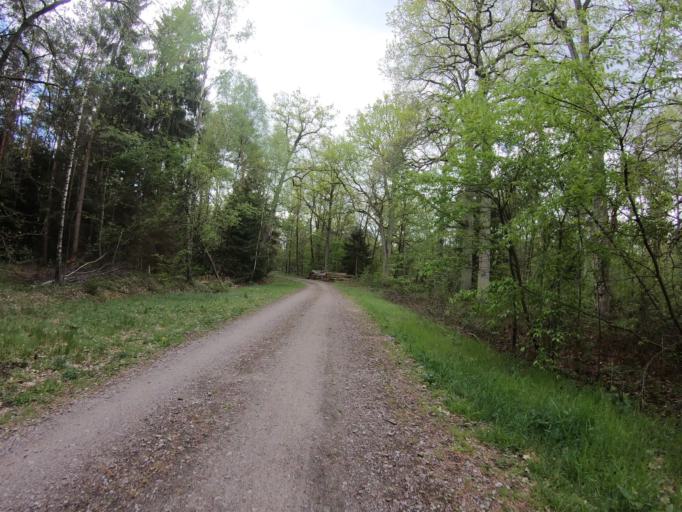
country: DE
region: Lower Saxony
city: Gifhorn
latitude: 52.5046
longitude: 10.5663
